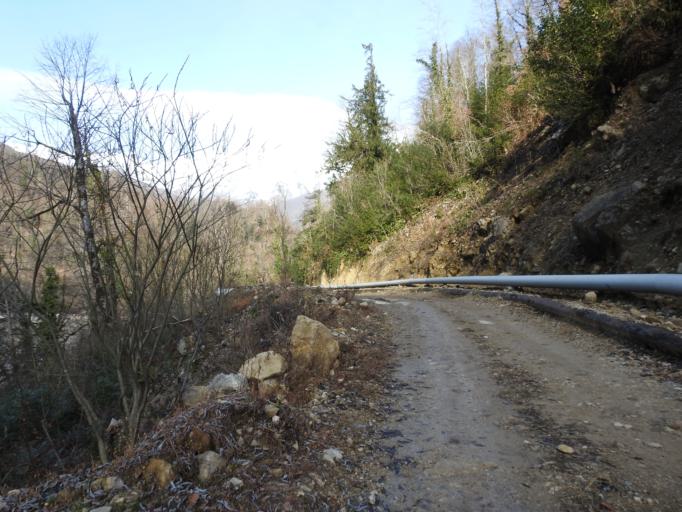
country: GE
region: Abkhazia
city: Gudauta
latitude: 43.2595
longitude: 40.6547
